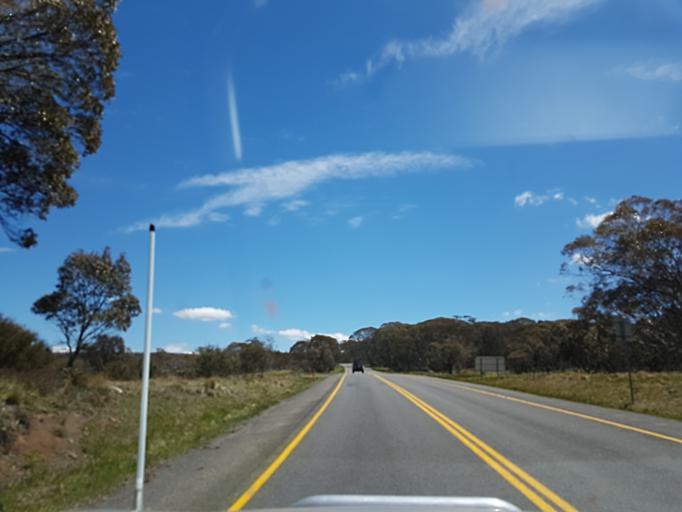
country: AU
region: Victoria
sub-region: Alpine
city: Mount Beauty
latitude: -37.0361
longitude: 147.3052
